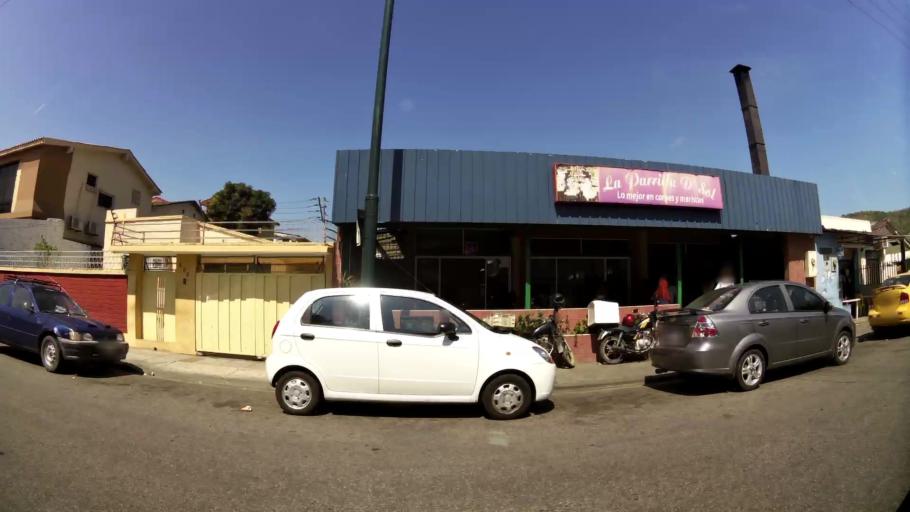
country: EC
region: Guayas
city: Guayaquil
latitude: -2.1636
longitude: -79.9197
